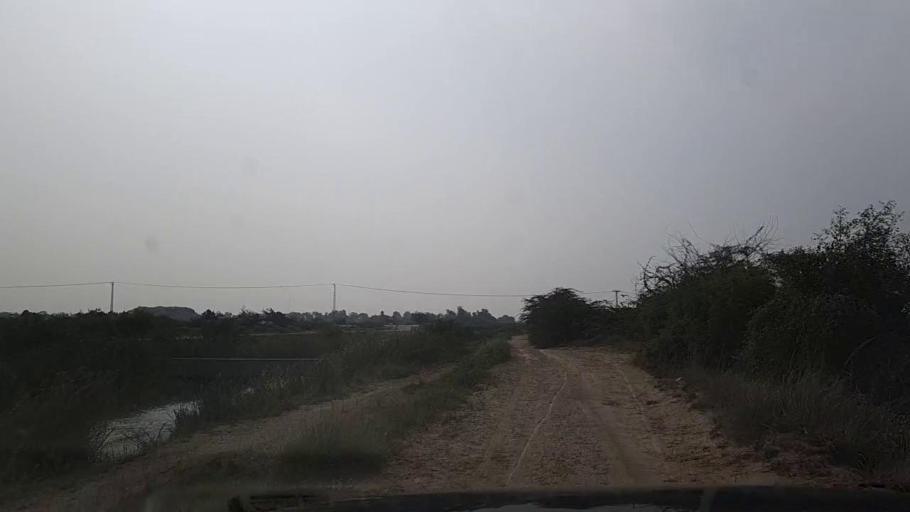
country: PK
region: Sindh
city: Thatta
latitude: 24.7443
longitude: 67.8063
